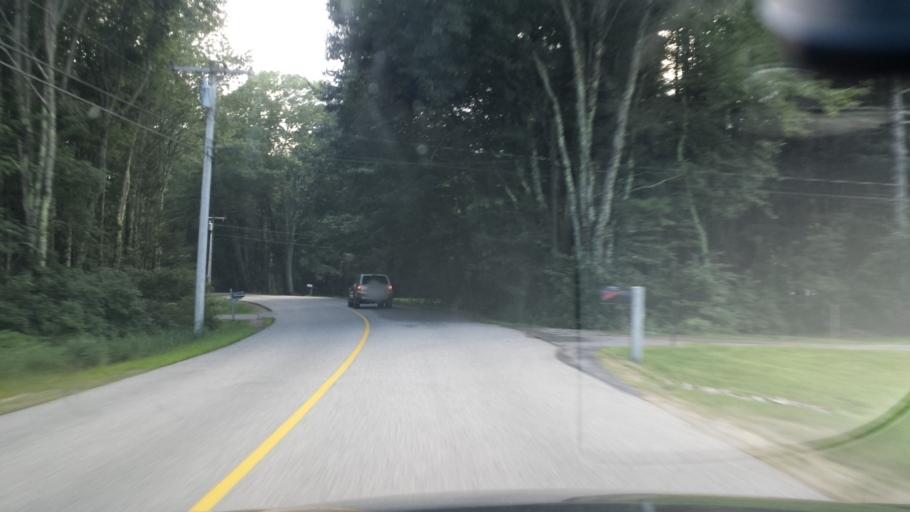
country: US
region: Maine
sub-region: York County
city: Arundel
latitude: 43.4321
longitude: -70.4543
